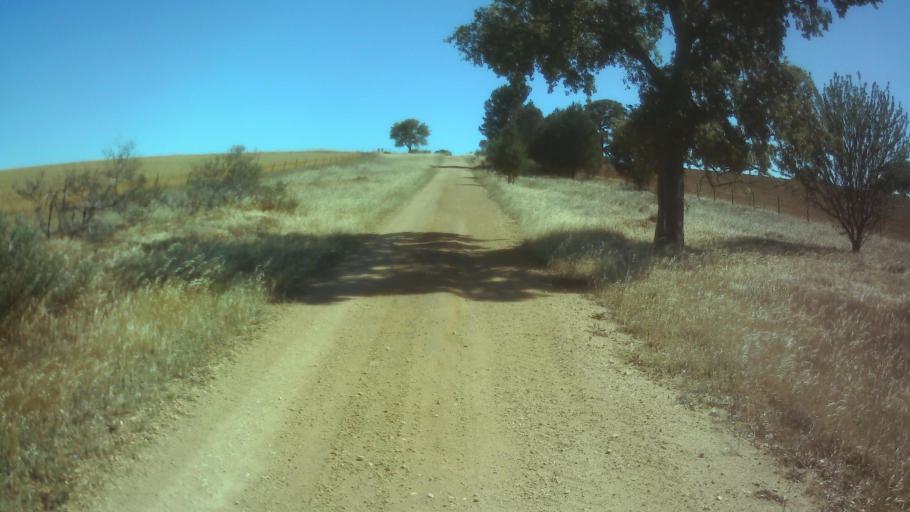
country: AU
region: New South Wales
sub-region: Weddin
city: Grenfell
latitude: -33.9712
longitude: 148.3436
